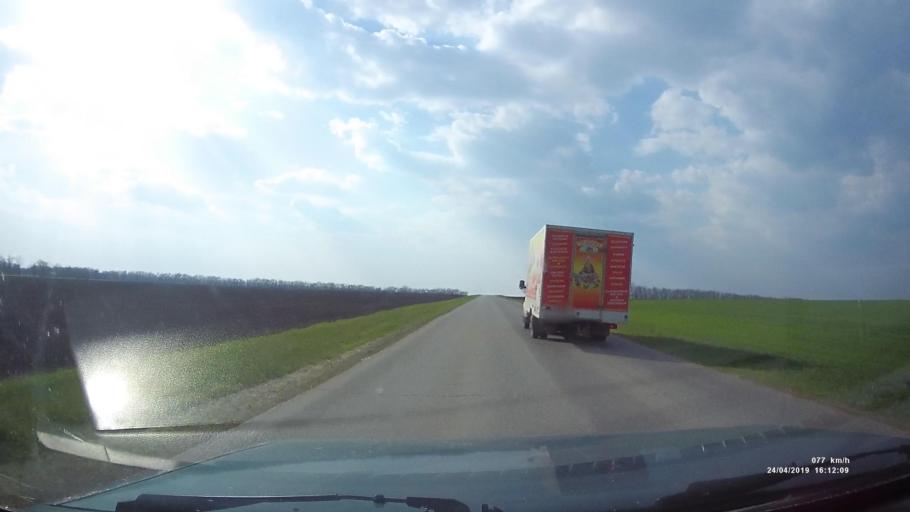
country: RU
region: Rostov
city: Sovetskoye
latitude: 46.7307
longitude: 42.2418
